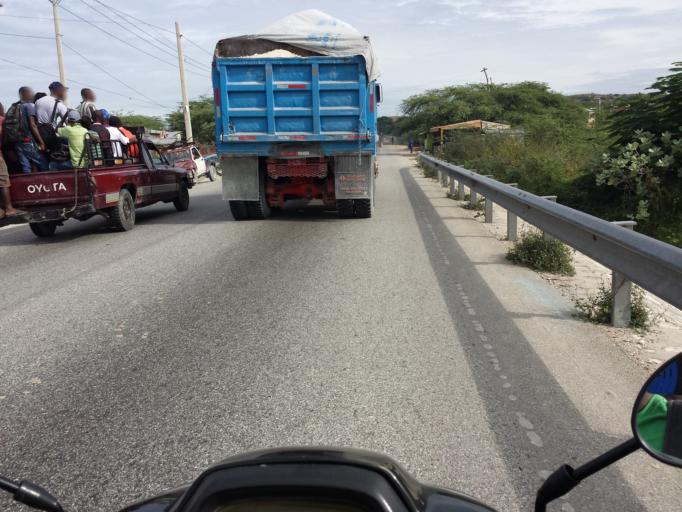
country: HT
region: Artibonite
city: Saint-Marc
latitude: 19.1382
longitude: -72.6720
